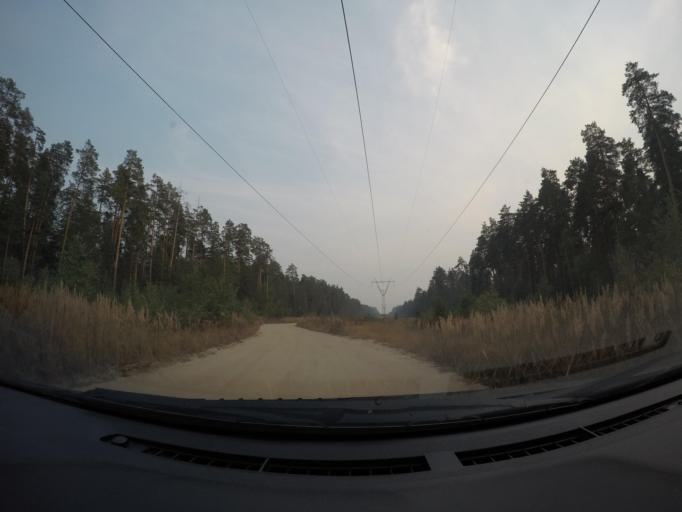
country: RU
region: Moskovskaya
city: Imeni Tsyurupy
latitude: 55.4995
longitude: 38.6878
